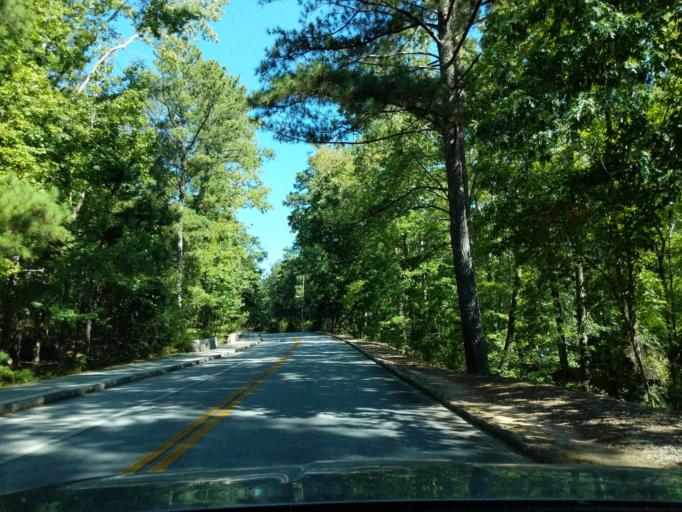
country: US
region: Georgia
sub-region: DeKalb County
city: Stone Mountain
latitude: 33.7988
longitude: -84.1476
